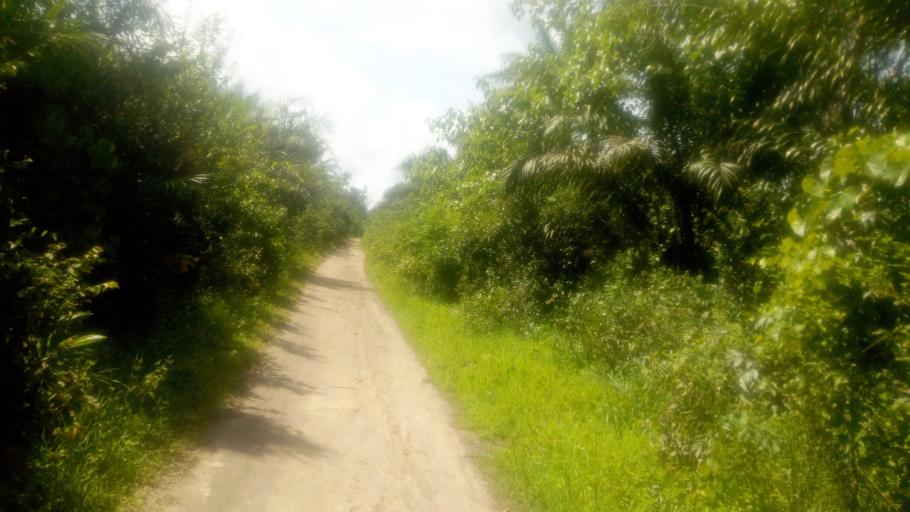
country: SL
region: Northern Province
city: Magburaka
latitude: 8.6539
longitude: -12.0692
